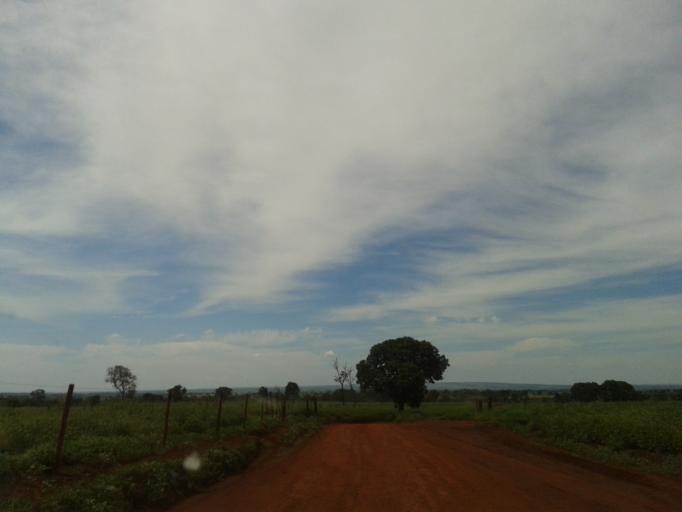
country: BR
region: Minas Gerais
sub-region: Capinopolis
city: Capinopolis
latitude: -18.7410
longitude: -49.8449
